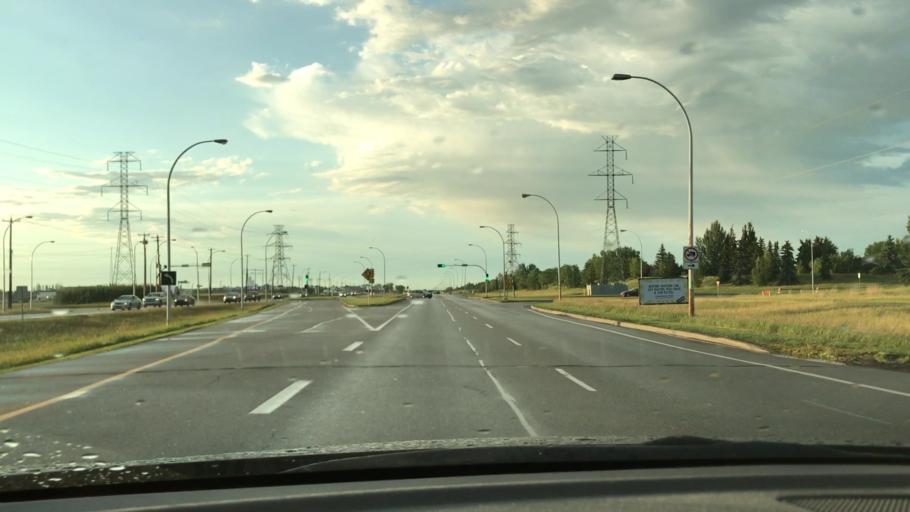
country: CA
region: Alberta
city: Edmonton
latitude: 53.4575
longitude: -113.4663
